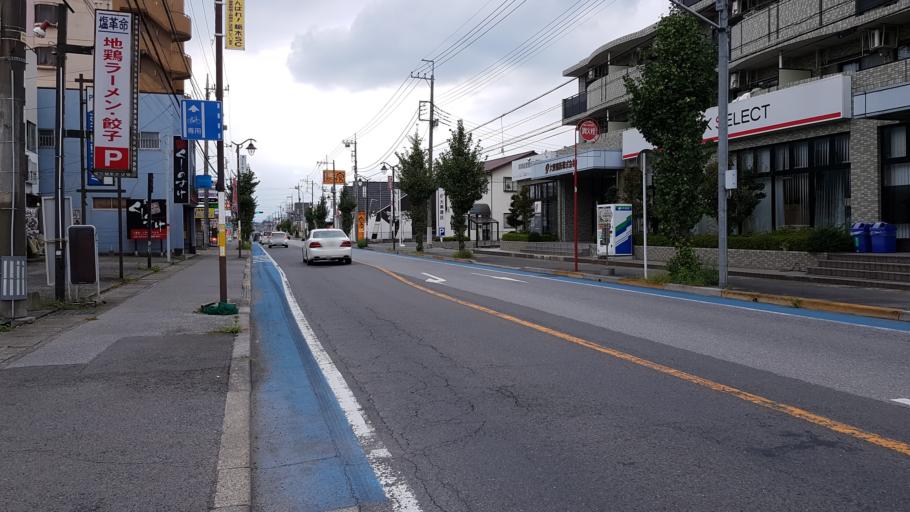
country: JP
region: Tochigi
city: Utsunomiya-shi
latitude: 36.5705
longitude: 139.9252
